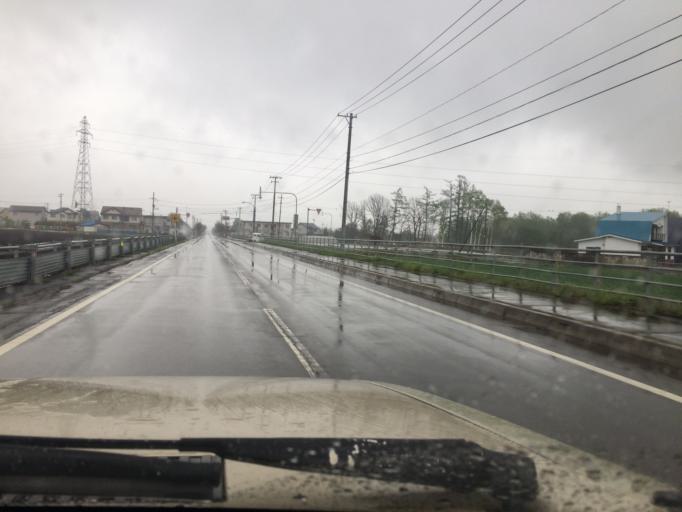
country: JP
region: Hokkaido
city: Obihiro
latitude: 42.8963
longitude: 143.0440
